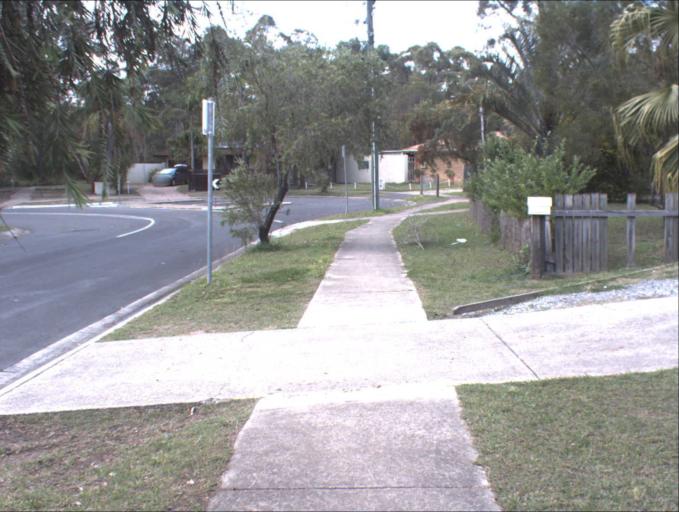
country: AU
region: Queensland
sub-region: Logan
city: Woodridge
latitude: -27.6713
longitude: 153.0571
